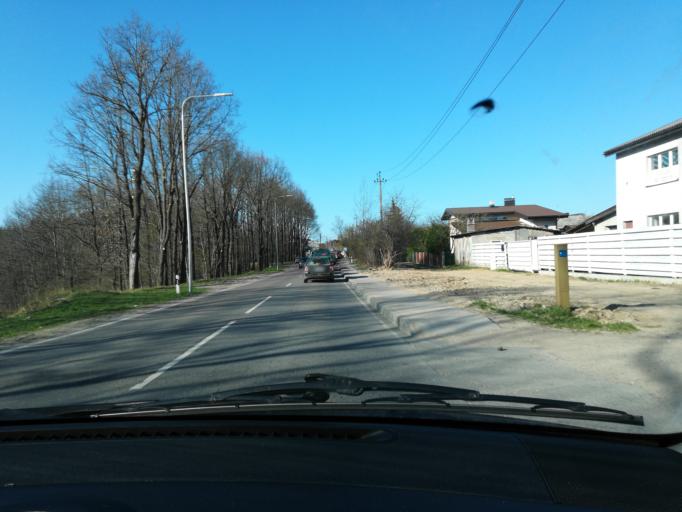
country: LT
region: Vilnius County
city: Rasos
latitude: 54.6596
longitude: 25.3372
